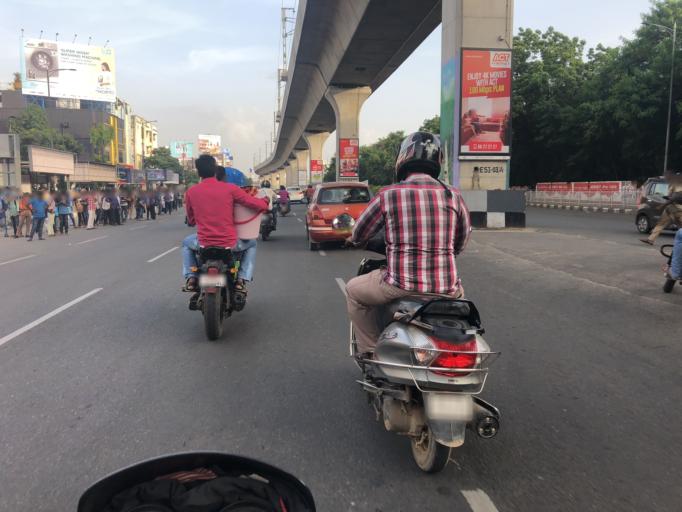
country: IN
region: Telangana
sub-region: Rangareddi
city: Kukatpalli
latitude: 17.4466
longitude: 78.4388
